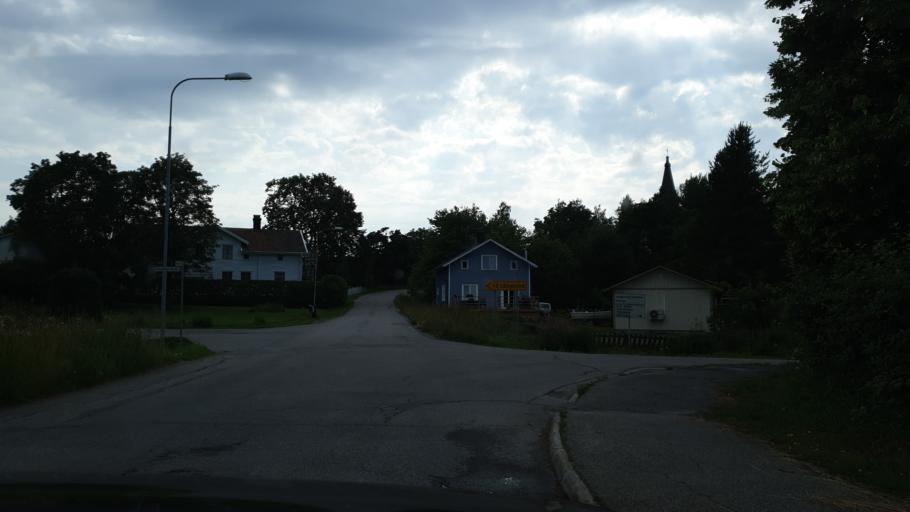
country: SE
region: Gaevleborg
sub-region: Hudiksvalls Kommun
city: Iggesund
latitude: 61.5443
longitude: 17.0038
